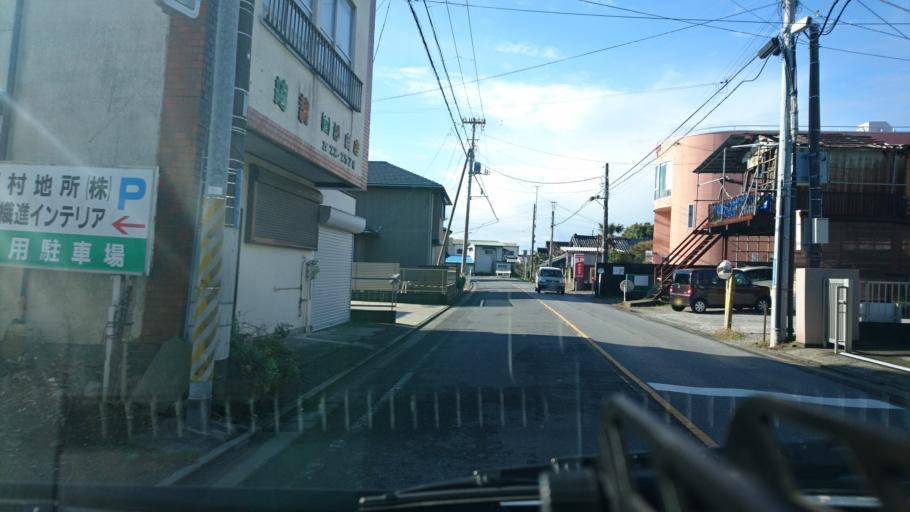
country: JP
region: Chiba
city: Kisarazu
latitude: 35.3775
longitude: 139.9222
